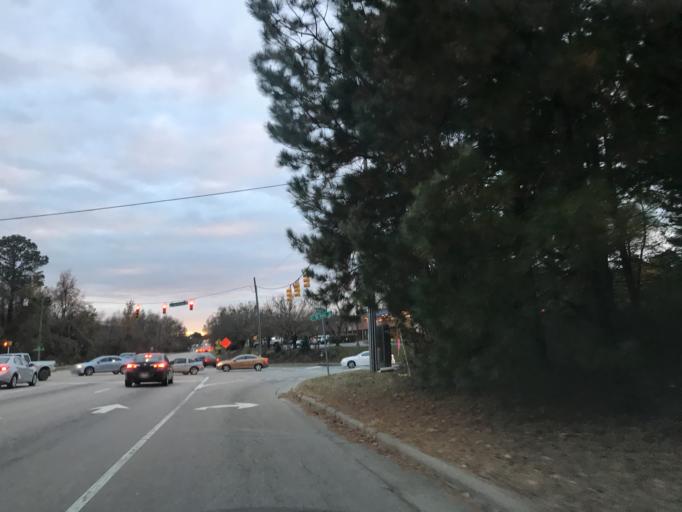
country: US
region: North Carolina
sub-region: Wake County
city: Raleigh
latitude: 35.8176
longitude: -78.6162
